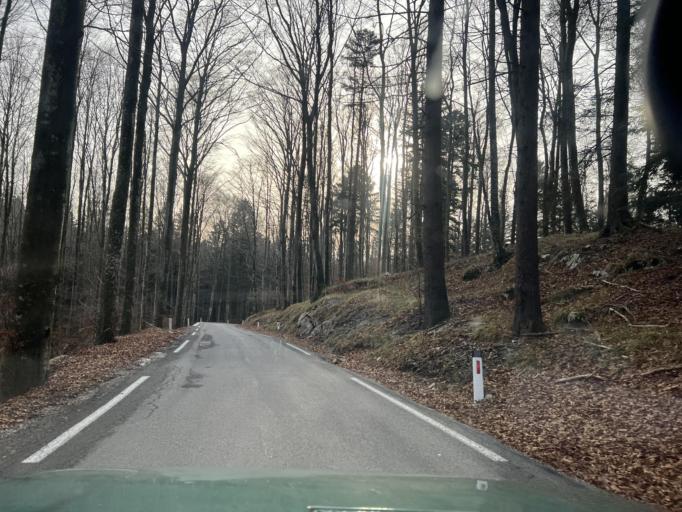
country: SI
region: Nova Gorica
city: Sempas
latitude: 45.9886
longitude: 13.7616
